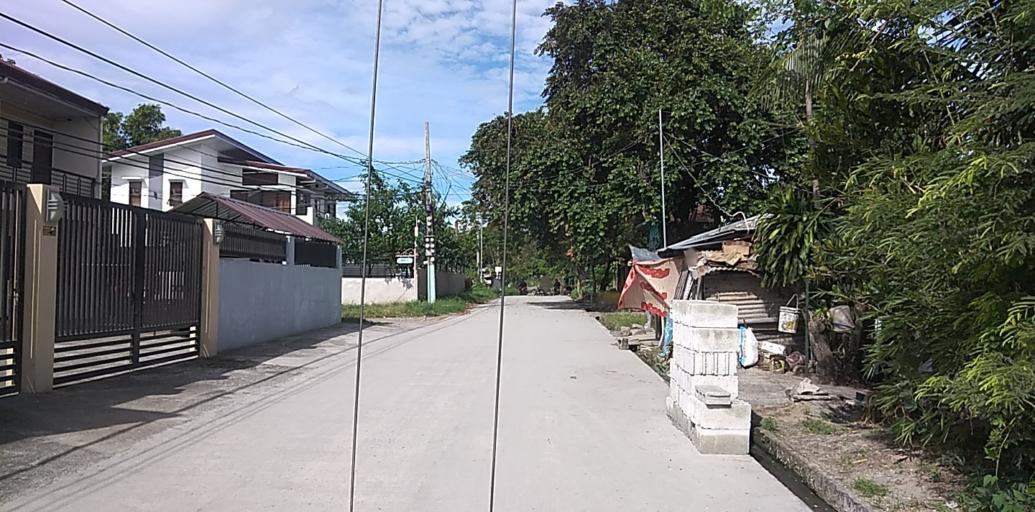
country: PH
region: Central Luzon
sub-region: Province of Pampanga
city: Angeles City
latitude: 15.1309
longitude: 120.5612
